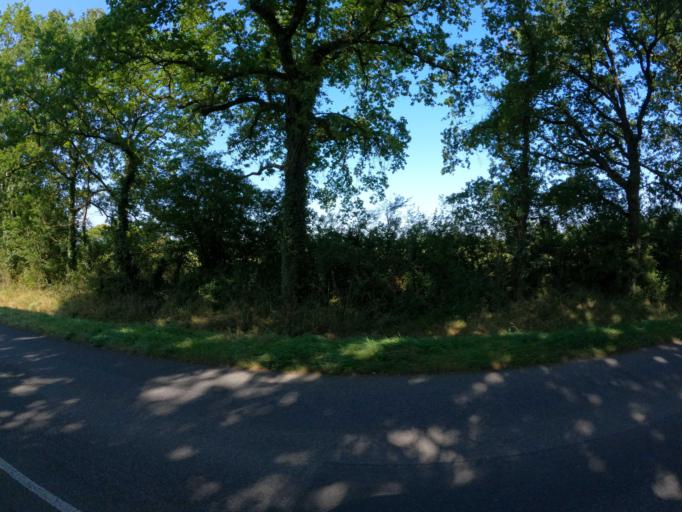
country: FR
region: Pays de la Loire
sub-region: Departement de la Loire-Atlantique
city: La Chevroliere
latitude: 47.0646
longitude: -1.5681
